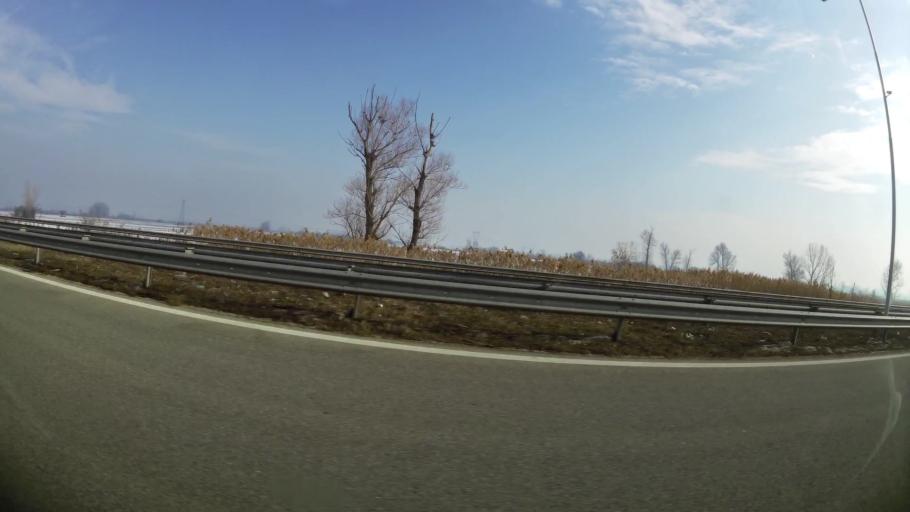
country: MK
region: Aracinovo
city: Arachinovo
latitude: 42.0036
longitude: 21.5344
